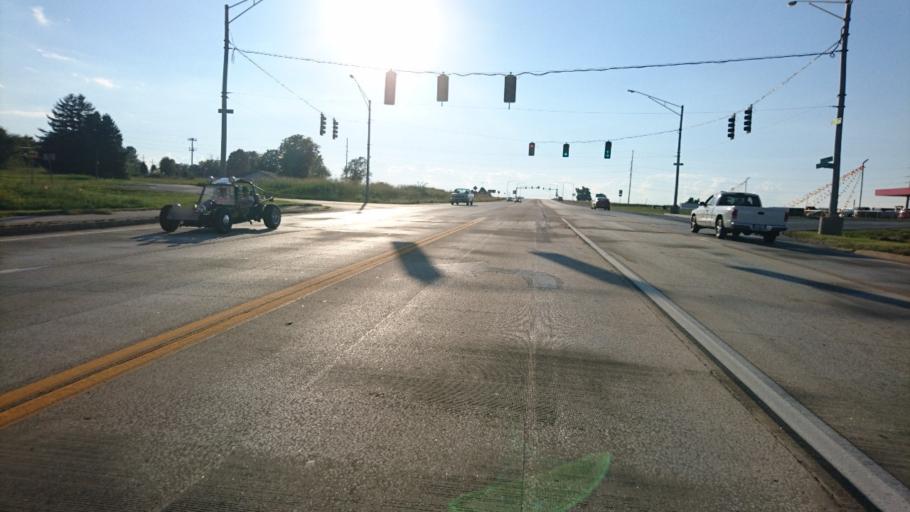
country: US
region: Missouri
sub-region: Greene County
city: Springfield
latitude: 37.2125
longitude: -93.3803
